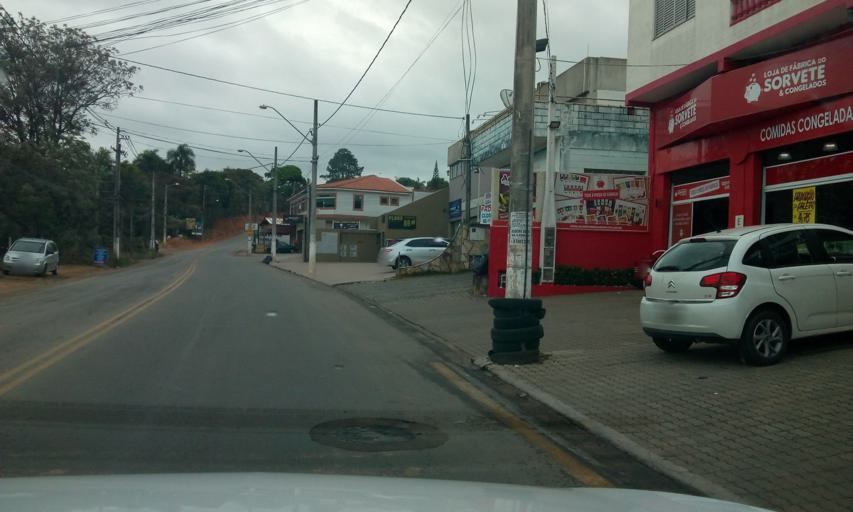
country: BR
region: Sao Paulo
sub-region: Itupeva
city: Itupeva
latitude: -23.1551
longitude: -47.0622
